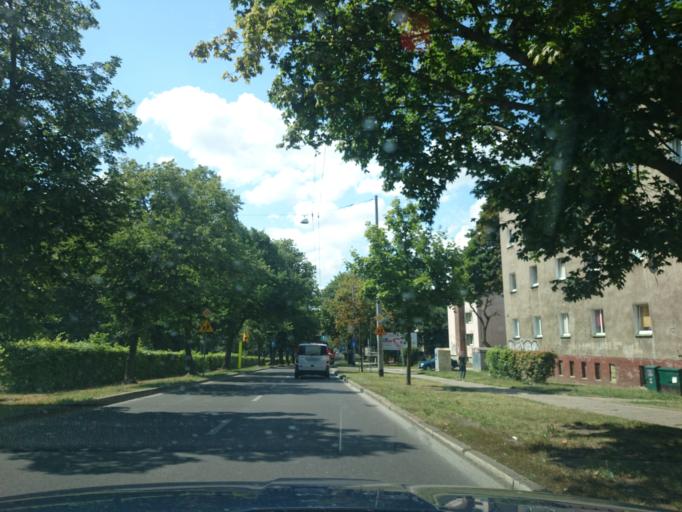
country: PL
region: West Pomeranian Voivodeship
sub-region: Szczecin
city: Szczecin
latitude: 53.4206
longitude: 14.5146
